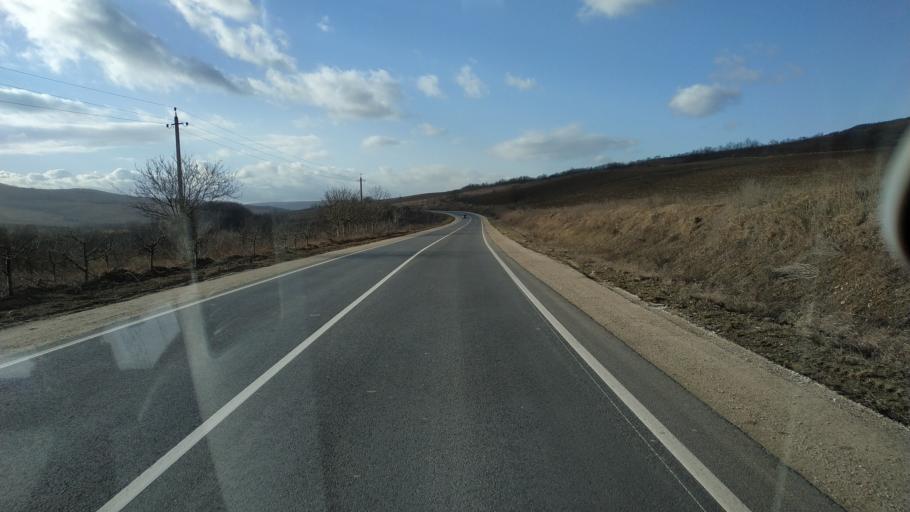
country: MD
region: Calarasi
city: Calarasi
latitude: 47.2929
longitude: 28.1731
